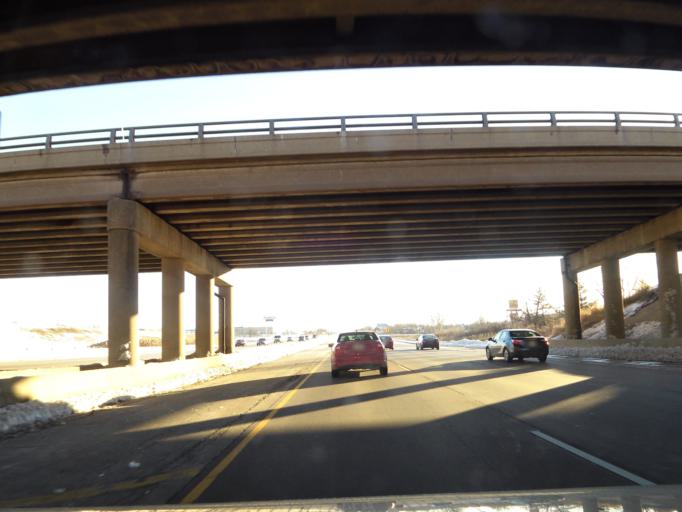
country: US
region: Wisconsin
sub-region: Racine County
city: Caledonia
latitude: 42.8728
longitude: -87.9373
